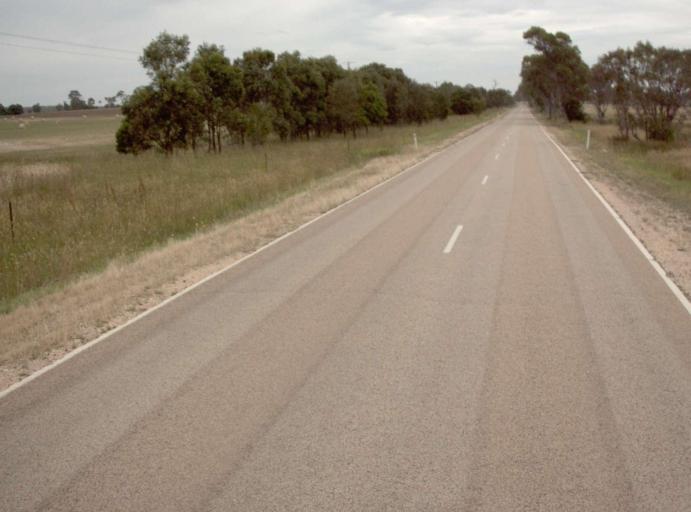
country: AU
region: Victoria
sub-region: East Gippsland
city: Bairnsdale
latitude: -37.8733
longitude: 147.4243
